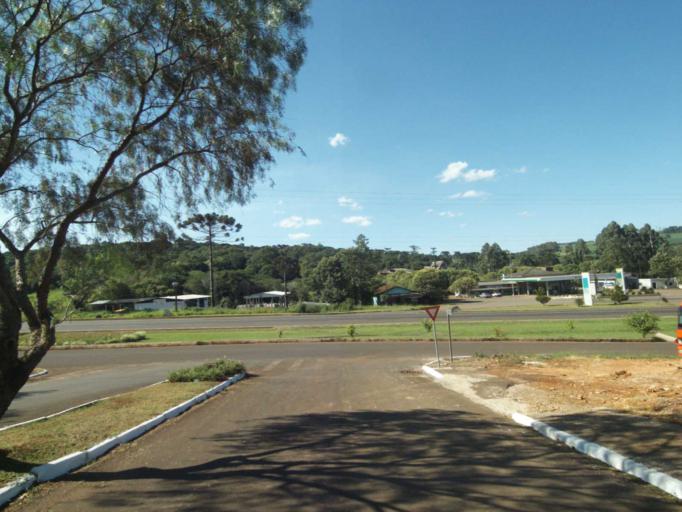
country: BR
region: Parana
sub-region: Laranjeiras Do Sul
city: Laranjeiras do Sul
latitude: -25.3790
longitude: -52.2037
